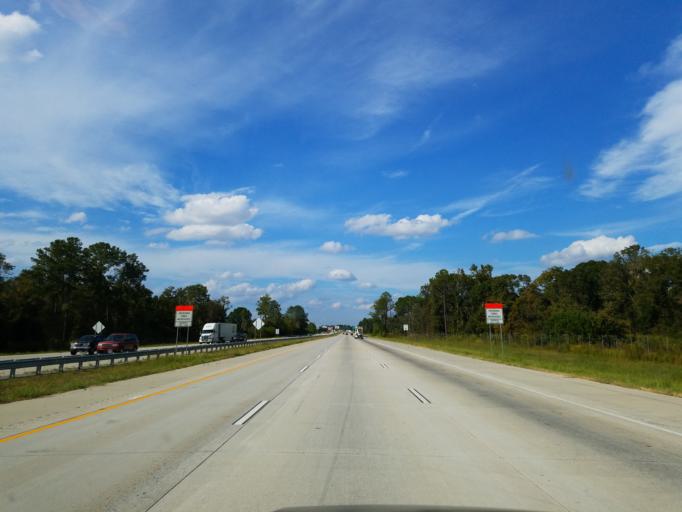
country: US
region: Georgia
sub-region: Dooly County
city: Vienna
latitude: 32.0977
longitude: -83.7630
